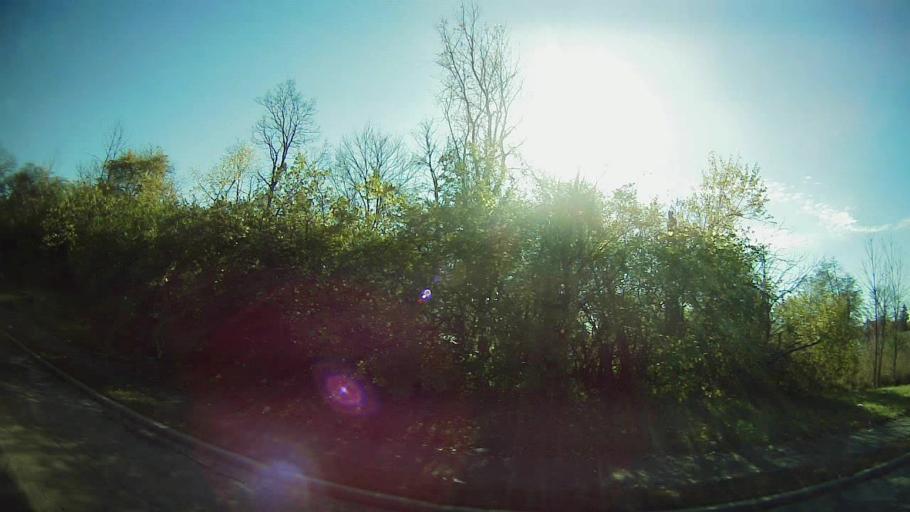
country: US
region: Michigan
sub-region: Wayne County
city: Dearborn Heights
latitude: 42.3571
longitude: -83.2650
